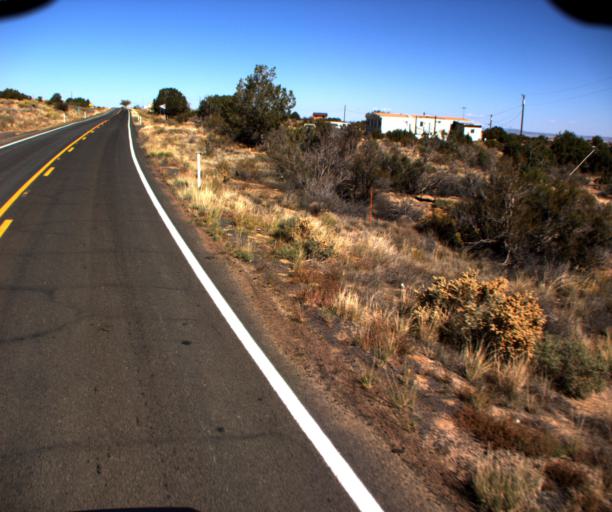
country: US
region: Arizona
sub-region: Navajo County
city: First Mesa
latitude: 35.9083
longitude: -110.6663
